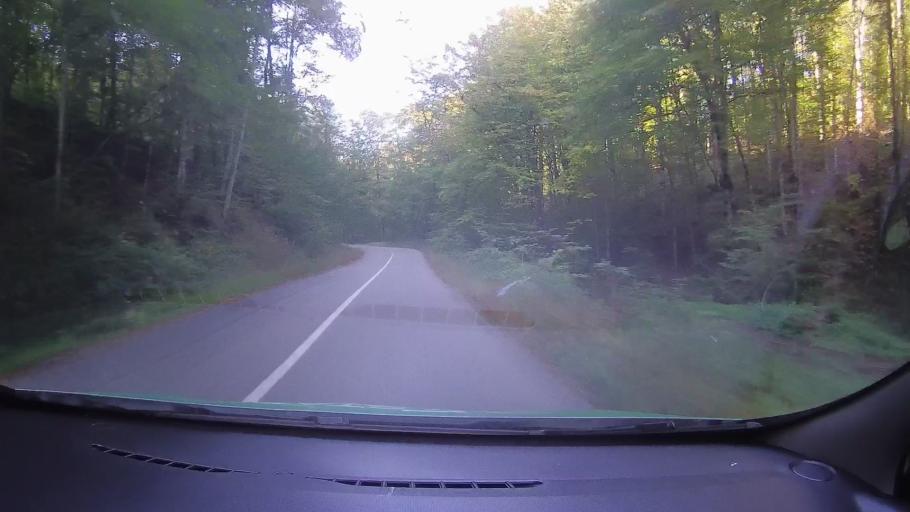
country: RO
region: Timis
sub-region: Comuna Nadrag
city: Nadrag
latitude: 45.6754
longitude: 22.1769
